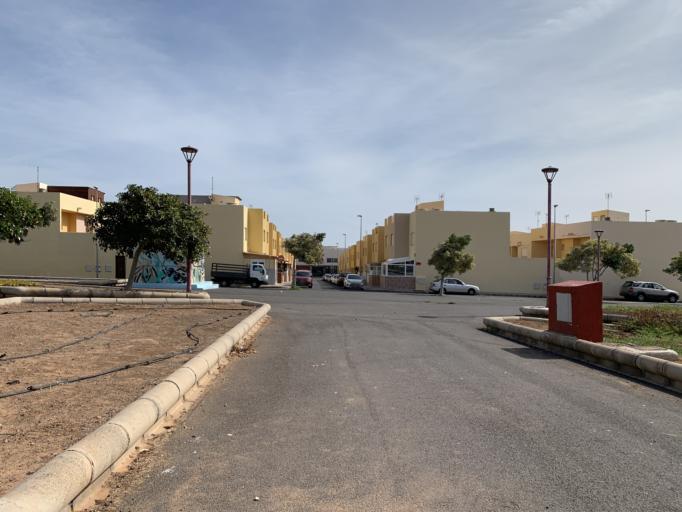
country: ES
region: Canary Islands
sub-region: Provincia de Las Palmas
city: Puerto del Rosario
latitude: 28.5106
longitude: -13.8610
